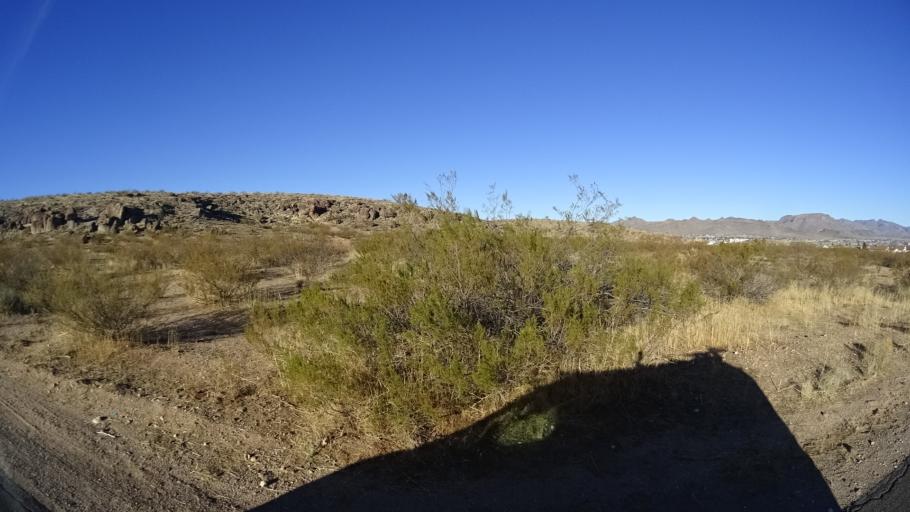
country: US
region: Arizona
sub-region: Mohave County
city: Kingman
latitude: 35.2080
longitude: -114.0024
